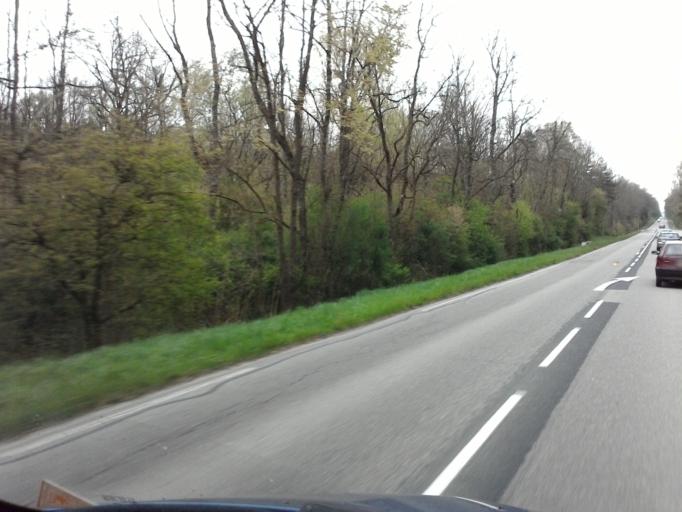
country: FR
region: Lorraine
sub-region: Departement de Meurthe-et-Moselle
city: Domgermain
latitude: 48.6416
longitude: 5.8652
